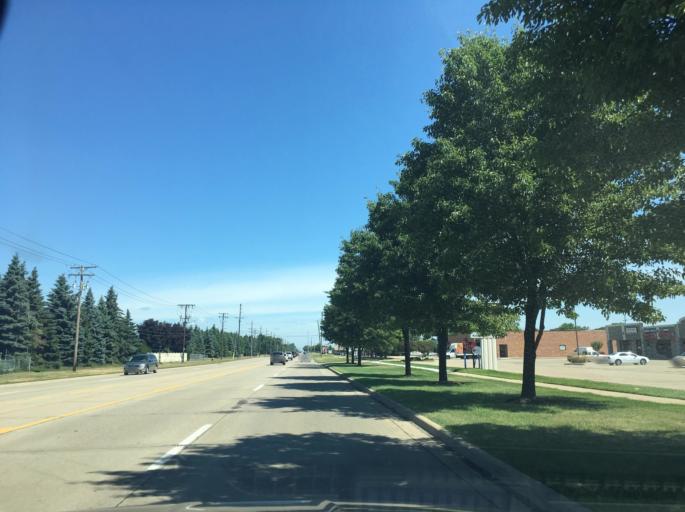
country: US
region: Michigan
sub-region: Macomb County
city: Clinton
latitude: 42.5902
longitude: -82.9717
